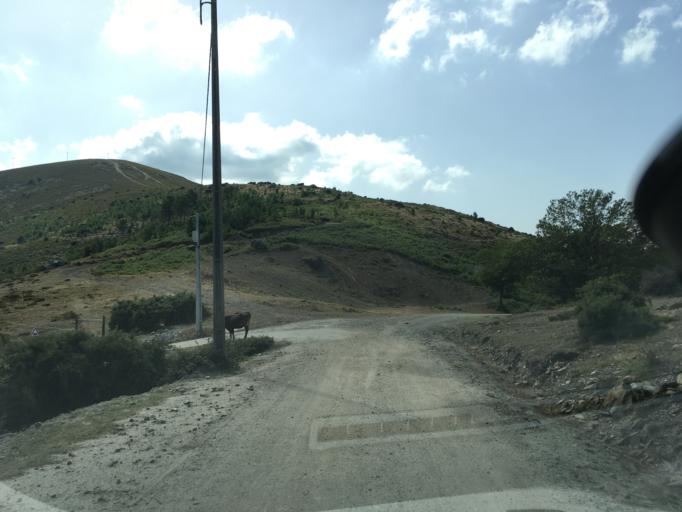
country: PT
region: Braga
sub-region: Celorico de Basto
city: Celorico de Basto
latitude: 41.3059
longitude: -7.9496
